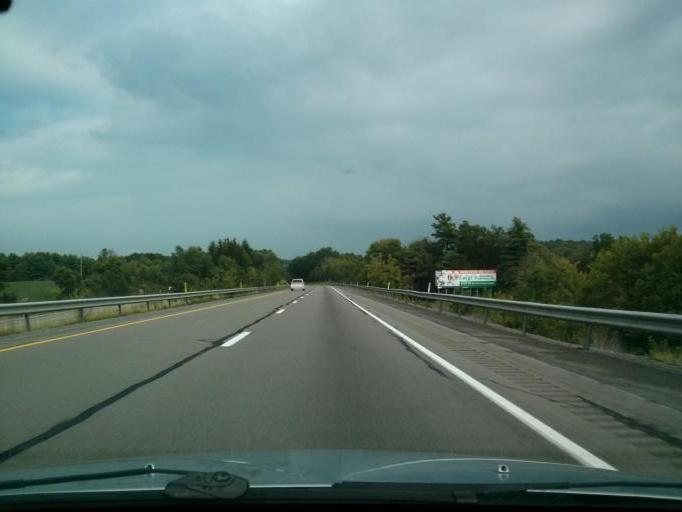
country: US
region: Pennsylvania
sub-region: Jefferson County
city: Brookville
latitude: 41.1736
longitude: -79.1112
